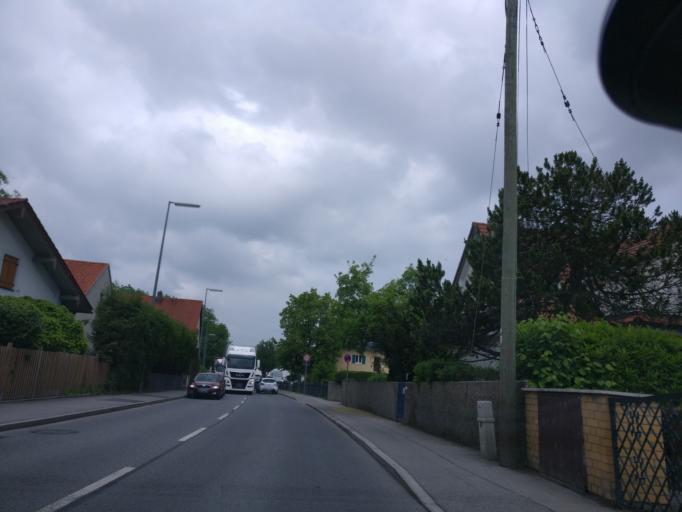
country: DE
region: Bavaria
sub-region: Upper Bavaria
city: Karlsfeld
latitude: 48.2005
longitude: 11.4581
